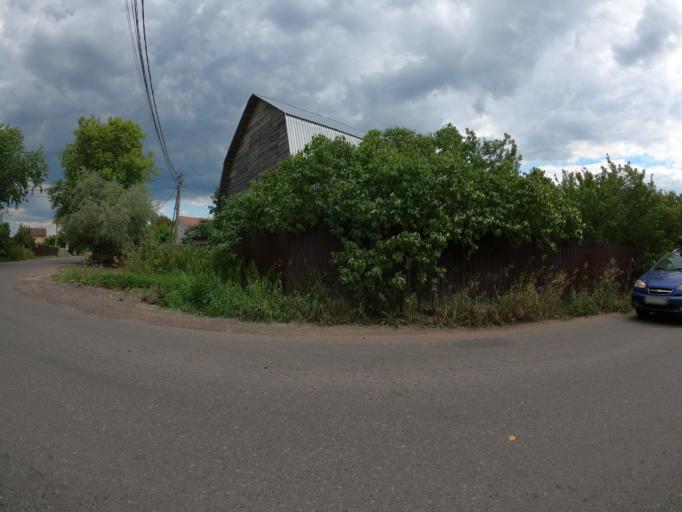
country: RU
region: Moskovskaya
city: Ramenskoye
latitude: 55.5417
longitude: 38.2314
